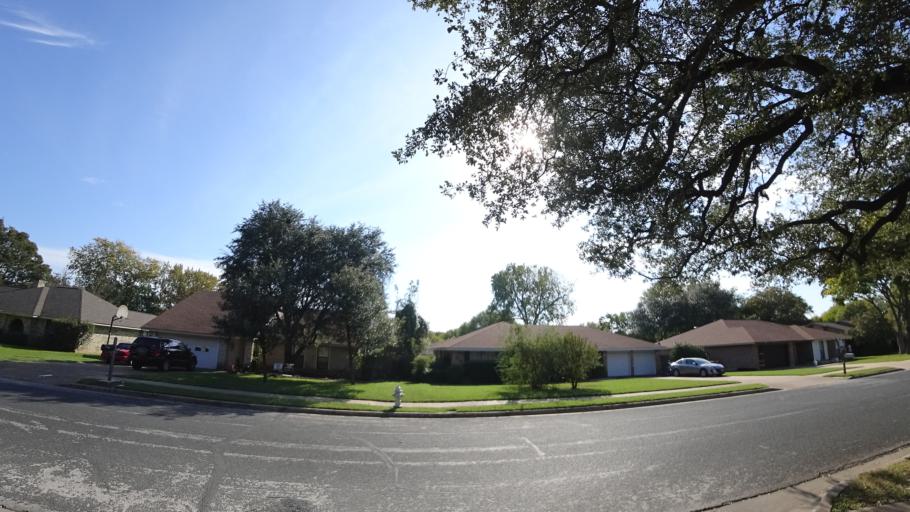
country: US
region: Texas
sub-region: Williamson County
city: Anderson Mill
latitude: 30.4492
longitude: -97.8071
